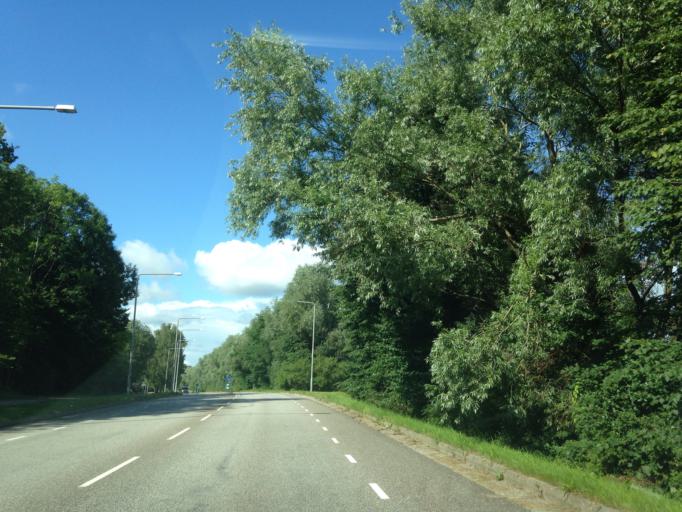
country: SE
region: Vaestra Goetaland
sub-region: Goteborg
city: Goeteborg
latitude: 57.7510
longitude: 11.9907
